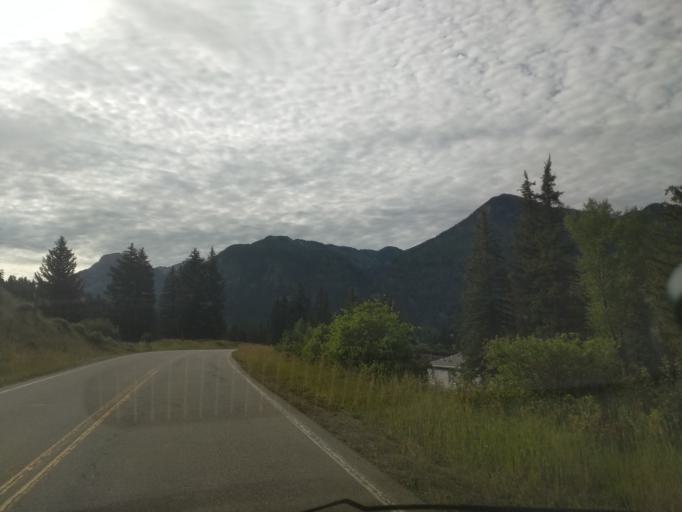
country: US
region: Colorado
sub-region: Gunnison County
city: Crested Butte
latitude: 39.0799
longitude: -107.2295
